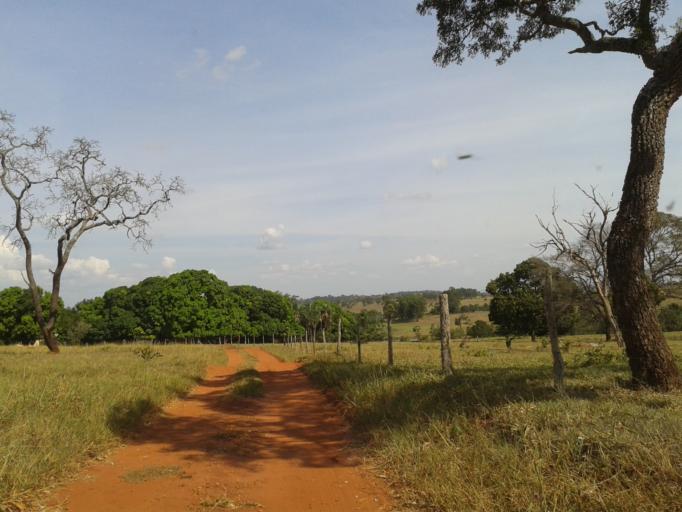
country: BR
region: Minas Gerais
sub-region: Campina Verde
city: Campina Verde
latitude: -19.5150
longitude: -49.5634
